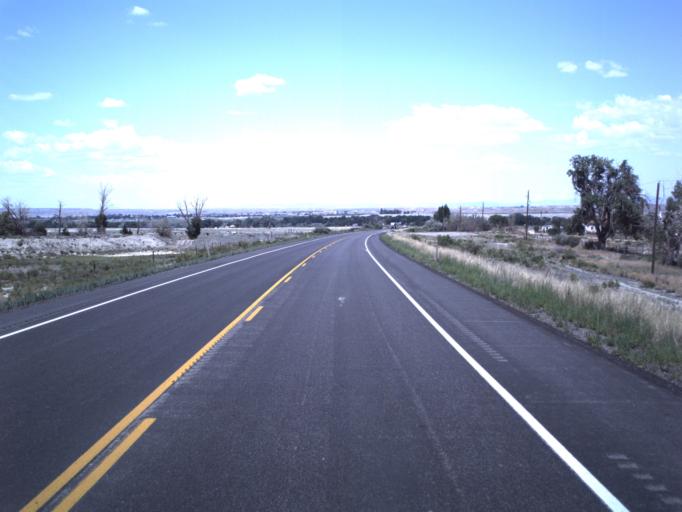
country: US
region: Utah
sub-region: Emery County
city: Huntington
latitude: 39.2841
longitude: -110.9736
